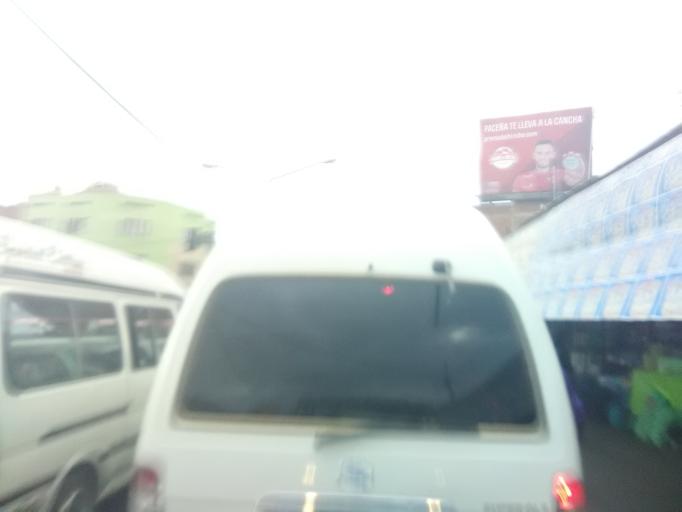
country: BO
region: Cochabamba
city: Cochabamba
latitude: -17.3987
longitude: -66.1525
